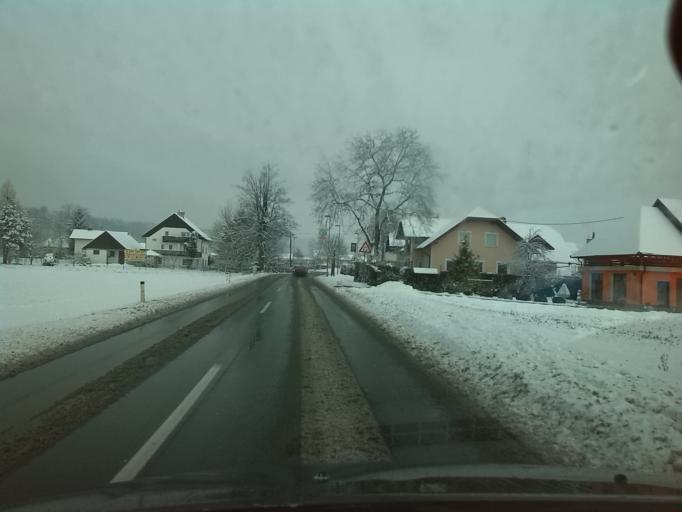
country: SI
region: Kamnik
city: Smarca
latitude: 46.2018
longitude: 14.5749
